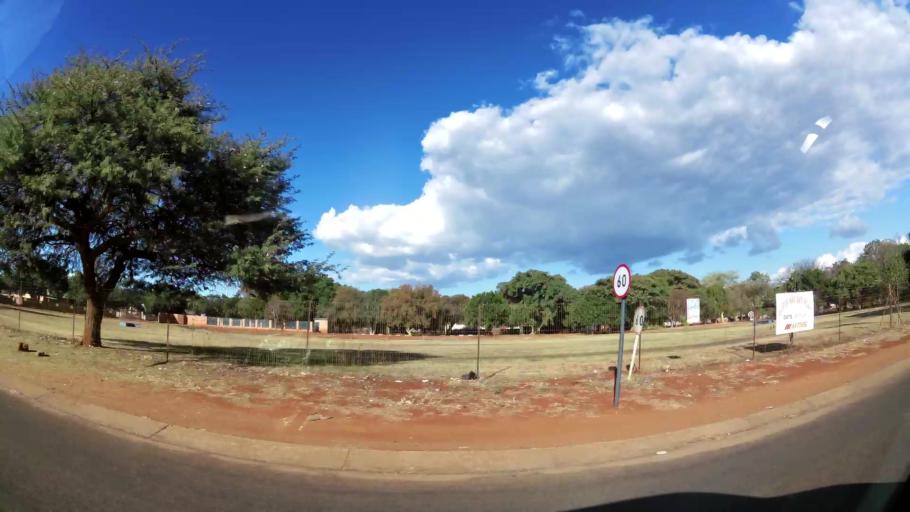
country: ZA
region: Limpopo
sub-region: Waterberg District Municipality
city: Mokopane
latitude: -24.1936
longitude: 29.0048
